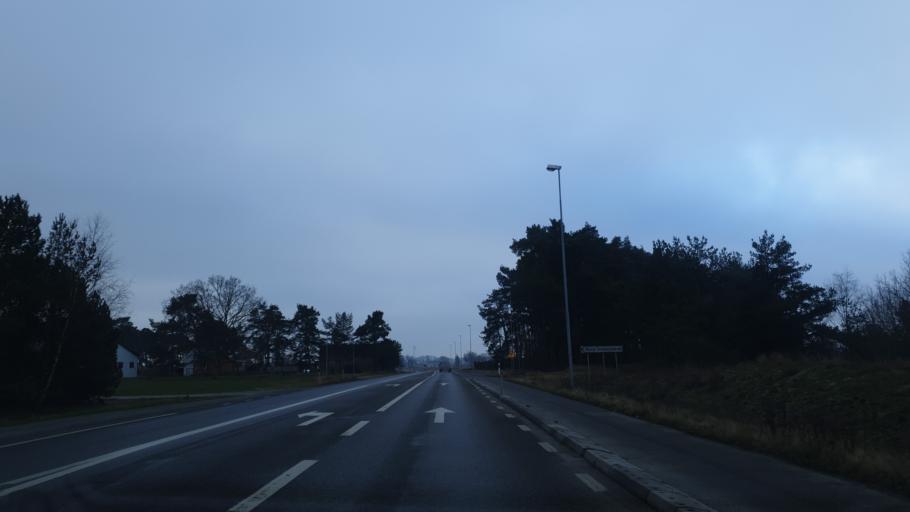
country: SE
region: Blekinge
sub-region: Solvesborgs Kommun
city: Soelvesborg
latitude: 56.0870
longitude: 14.6480
